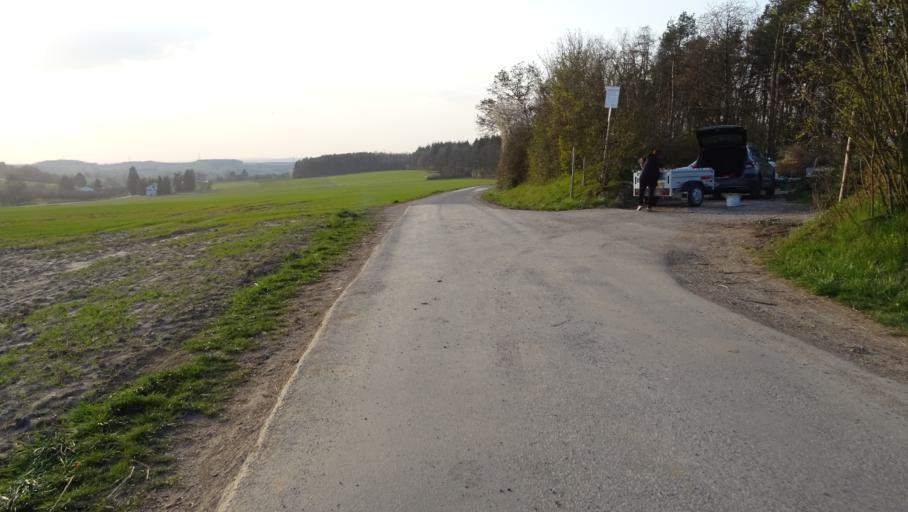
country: DE
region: Baden-Wuerttemberg
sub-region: Regierungsbezirk Stuttgart
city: Roigheim
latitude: 49.3981
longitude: 9.2986
